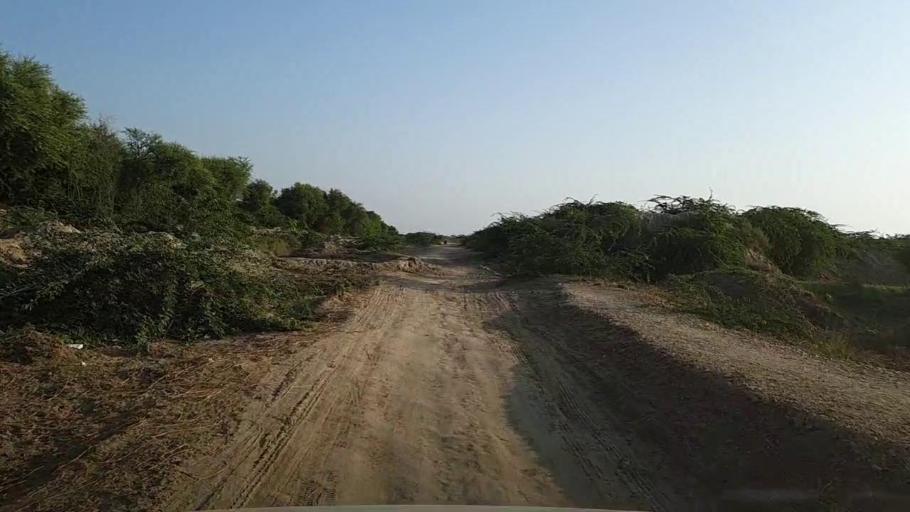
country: PK
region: Sindh
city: Kario
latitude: 24.7115
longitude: 68.6669
